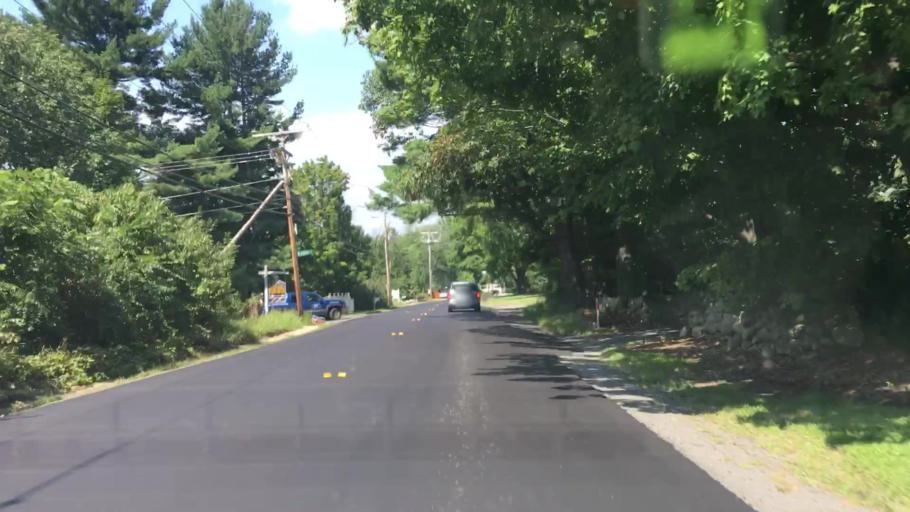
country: US
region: New Hampshire
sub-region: Rockingham County
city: Hampstead
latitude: 42.8968
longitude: -71.2143
